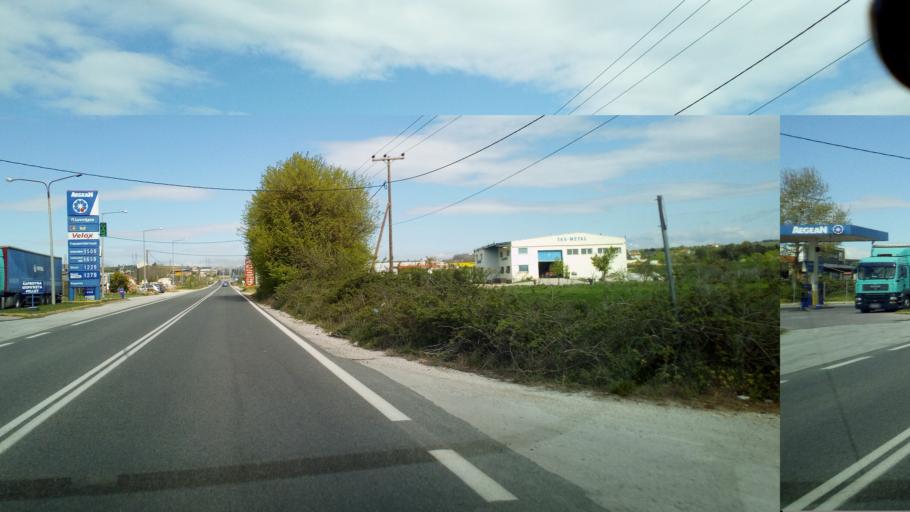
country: GR
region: Central Macedonia
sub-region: Nomos Thessalonikis
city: Drymos
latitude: 40.7706
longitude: 22.9511
